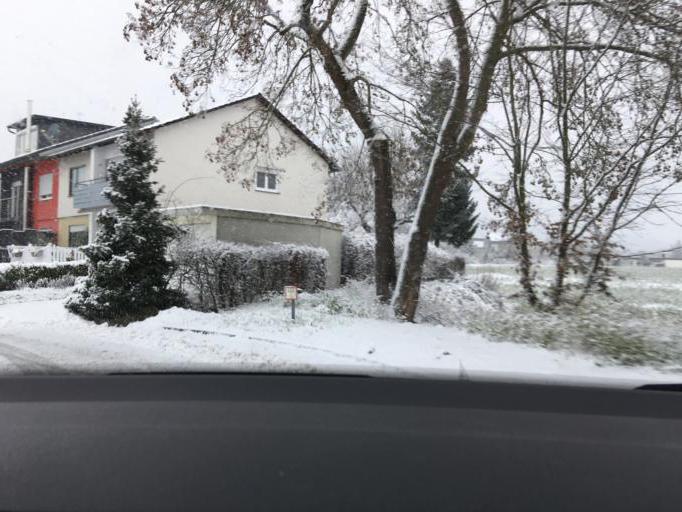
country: DE
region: Baden-Wuerttemberg
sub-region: Freiburg Region
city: Gottmadingen
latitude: 47.7319
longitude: 8.7916
